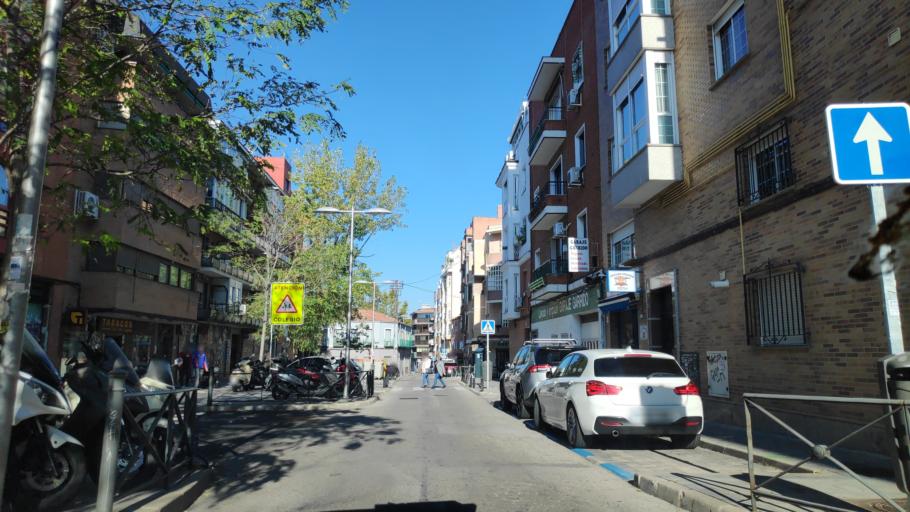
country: ES
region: Madrid
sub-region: Provincia de Madrid
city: Tetuan de las Victorias
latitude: 40.4670
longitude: -3.6970
